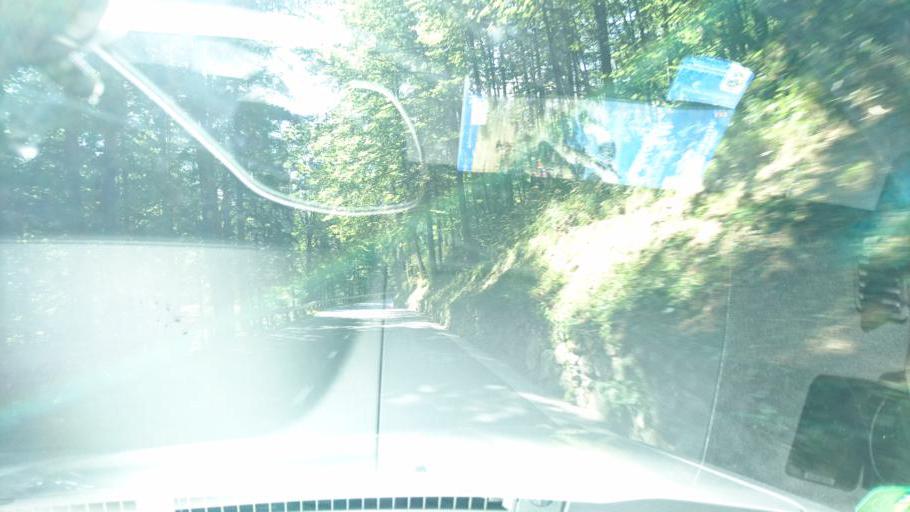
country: SI
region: Kranjska Gora
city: Kranjska Gora
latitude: 46.4546
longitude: 13.7798
